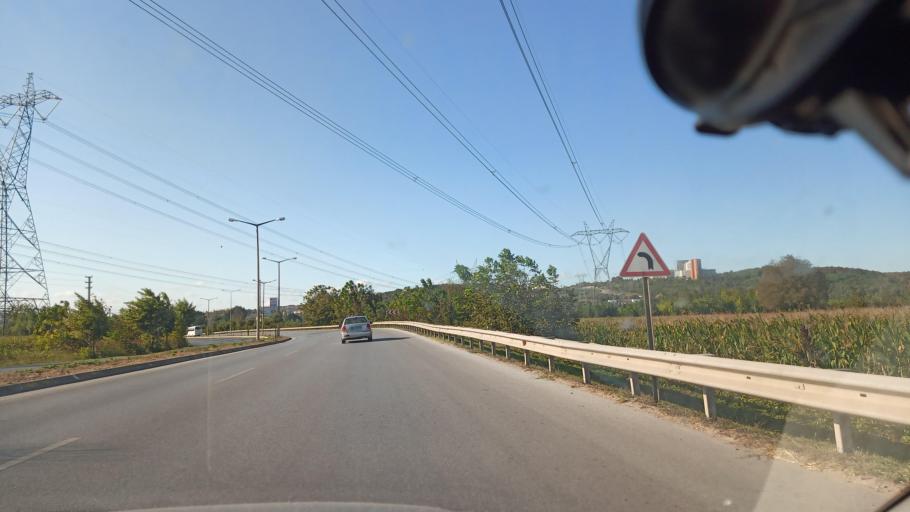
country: TR
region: Sakarya
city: Kazimpasa
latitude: 40.8369
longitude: 30.3450
